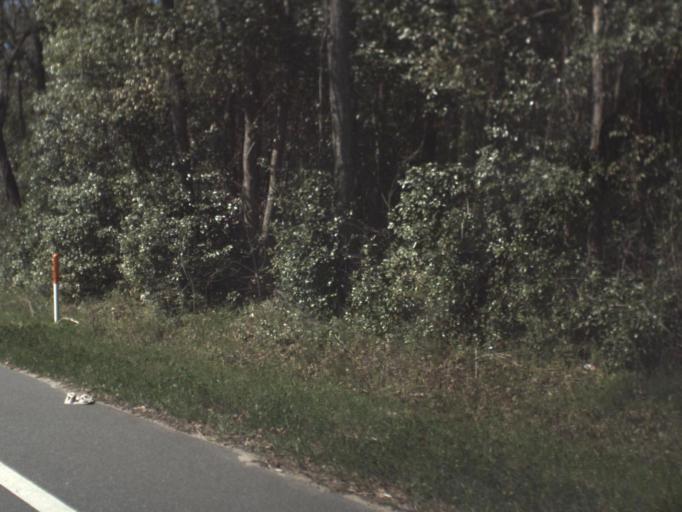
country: US
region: Florida
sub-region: Gadsden County
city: Chattahoochee
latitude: 30.6927
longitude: -84.7514
